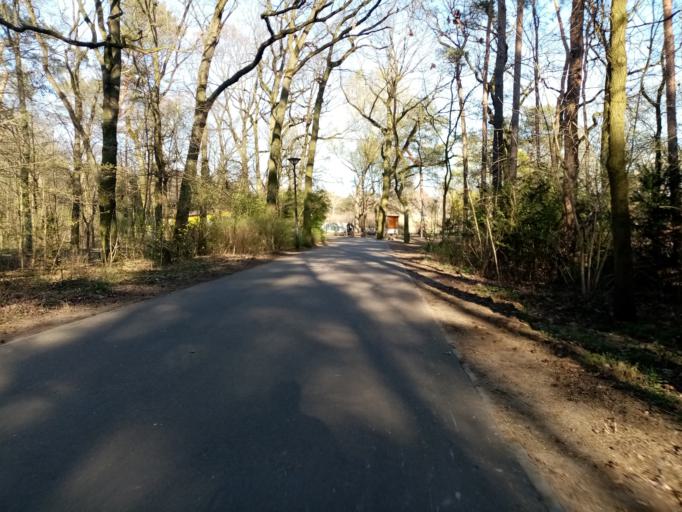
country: DE
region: Berlin
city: Karlshorst
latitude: 52.4638
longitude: 13.5457
